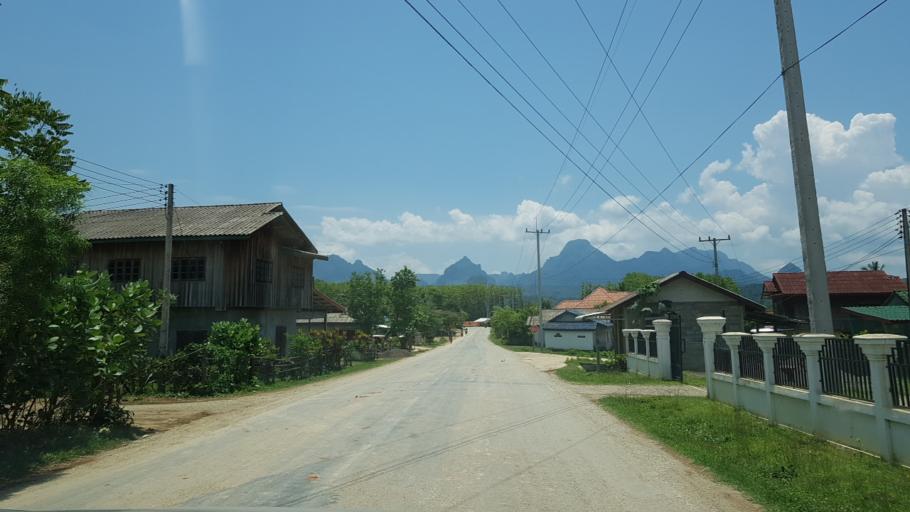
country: LA
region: Vientiane
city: Muang Kasi
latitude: 19.2529
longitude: 102.2370
